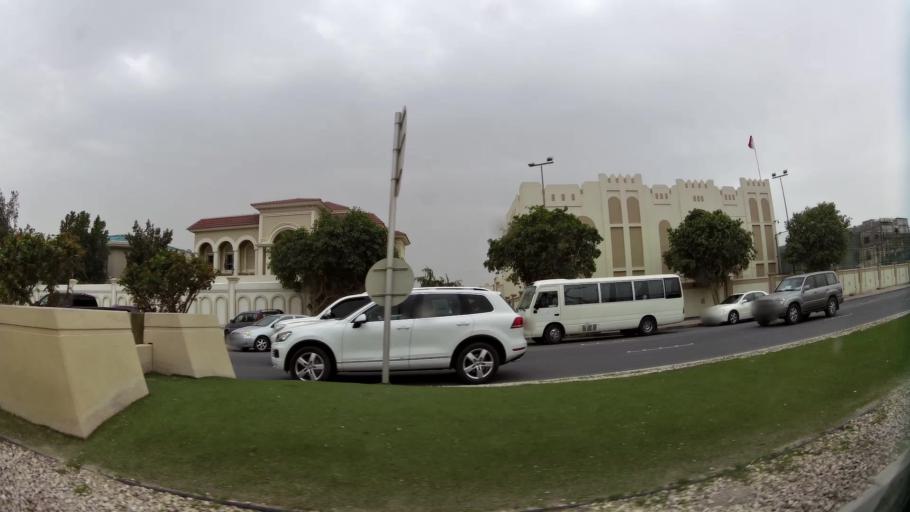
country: BH
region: Northern
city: Madinat `Isa
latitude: 26.1526
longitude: 50.5418
